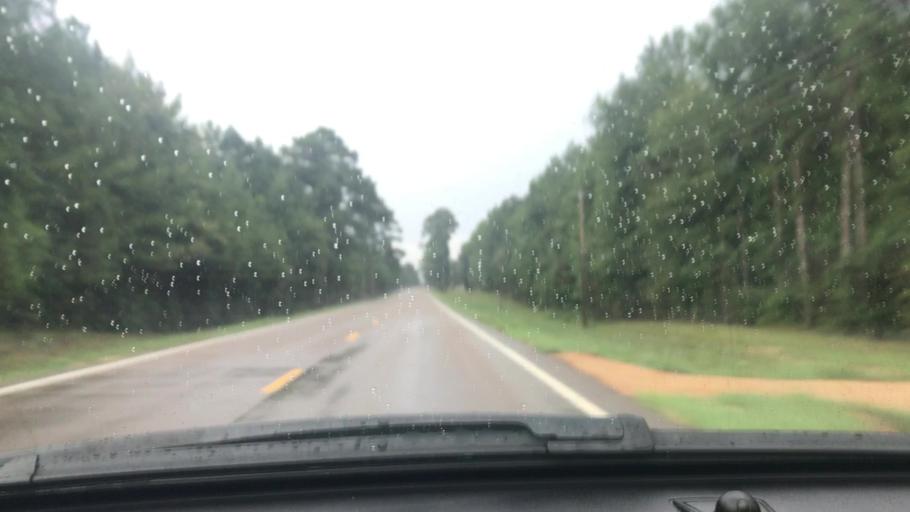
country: US
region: Mississippi
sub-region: Pike County
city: Summit
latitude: 31.3451
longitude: -90.5895
